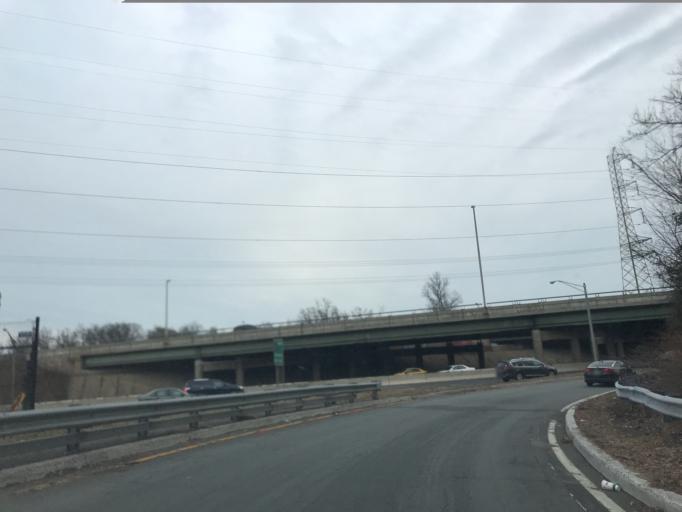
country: US
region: New Jersey
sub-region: Middlesex County
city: Metuchen
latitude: 40.5294
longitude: -74.3542
